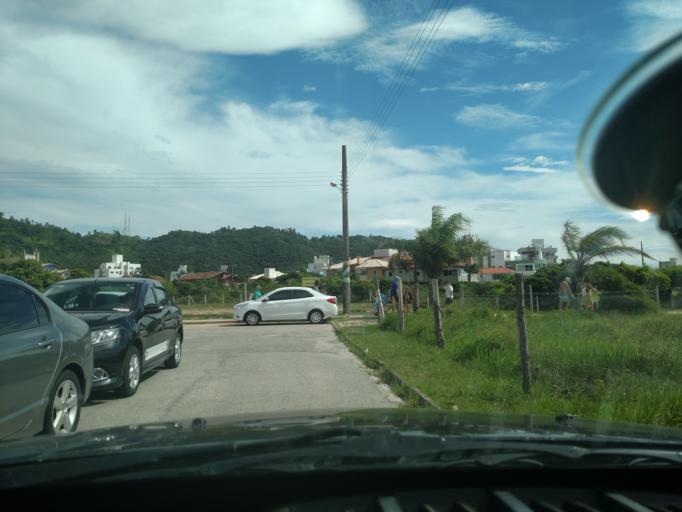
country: BR
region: Santa Catarina
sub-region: Tijucas
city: Tijucas
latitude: -27.3250
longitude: -48.5397
